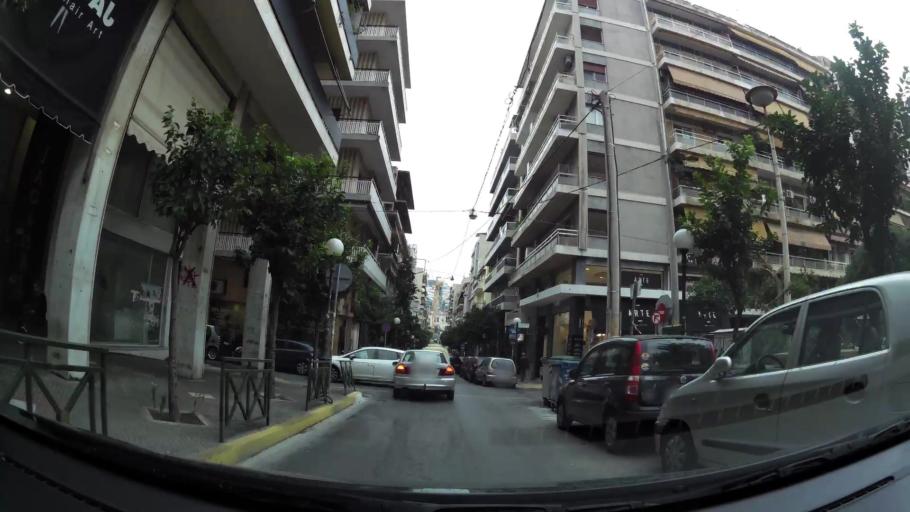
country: GR
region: Attica
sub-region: Nomos Attikis
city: Piraeus
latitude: 37.9433
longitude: 23.6488
